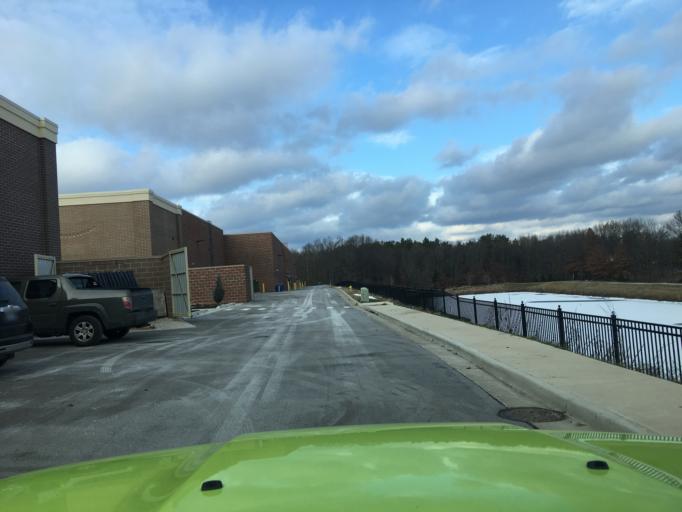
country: US
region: Michigan
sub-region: Kent County
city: Northview
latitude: 43.0012
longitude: -85.5879
